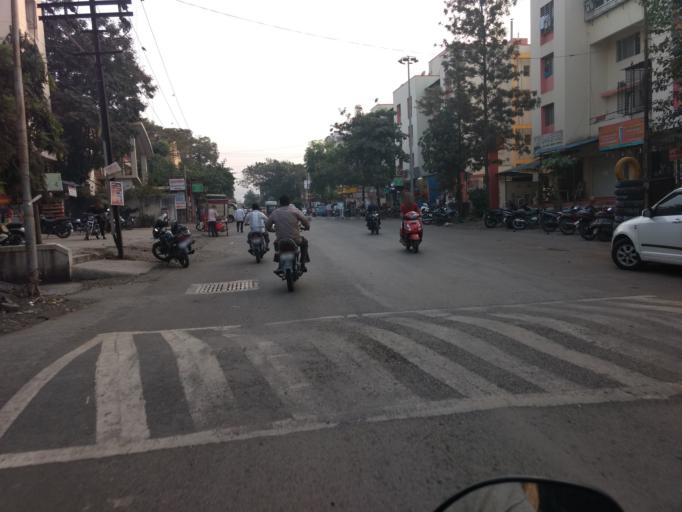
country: IN
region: Maharashtra
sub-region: Pune Division
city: Pune
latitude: 18.4584
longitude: 73.8695
